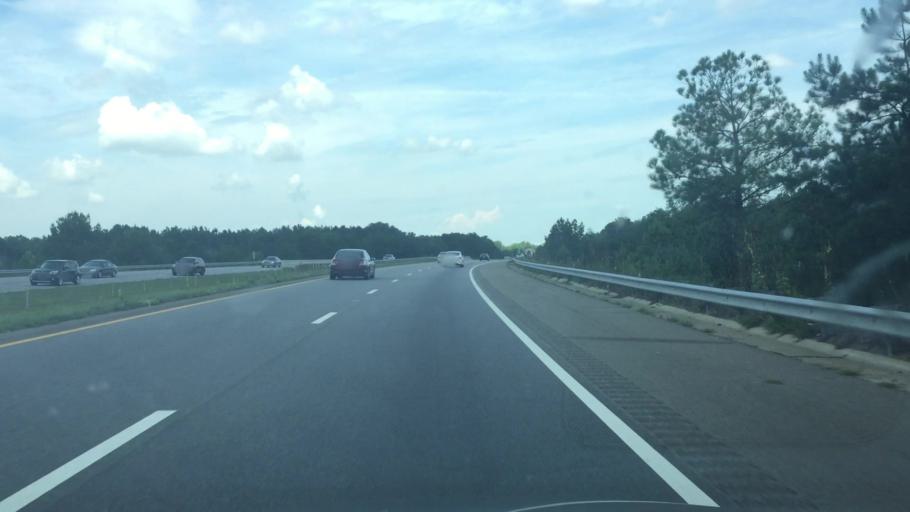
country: US
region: North Carolina
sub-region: Richmond County
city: Hamlet
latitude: 34.8535
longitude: -79.7358
